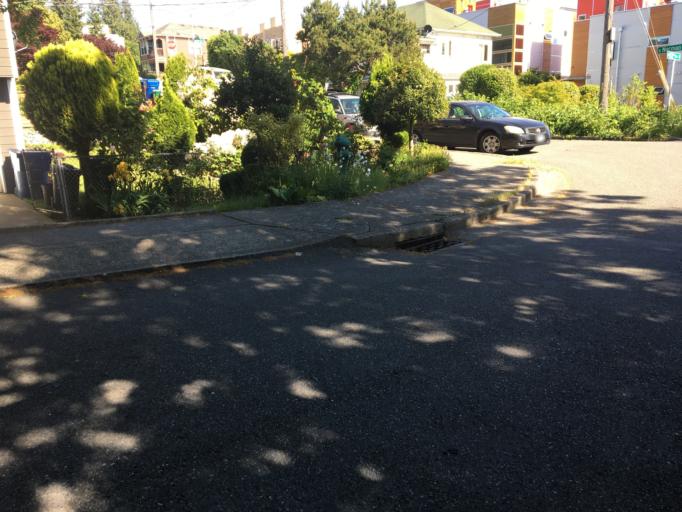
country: US
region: Washington
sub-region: King County
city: Seattle
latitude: 47.5932
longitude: -122.3032
